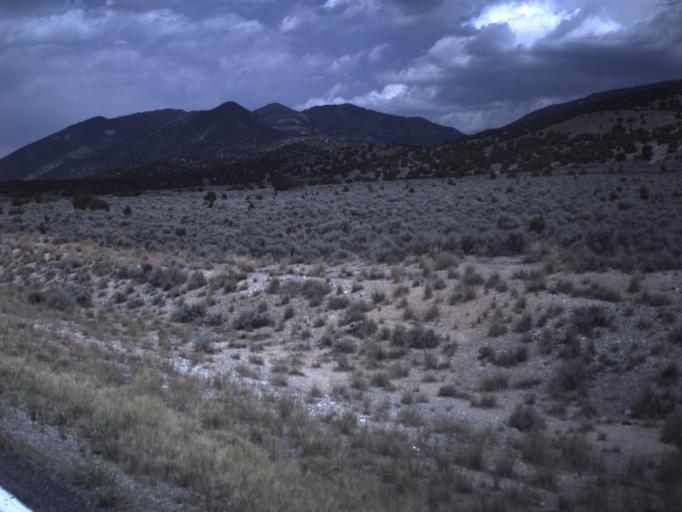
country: US
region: Utah
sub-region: Tooele County
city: Tooele
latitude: 40.3231
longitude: -112.2875
